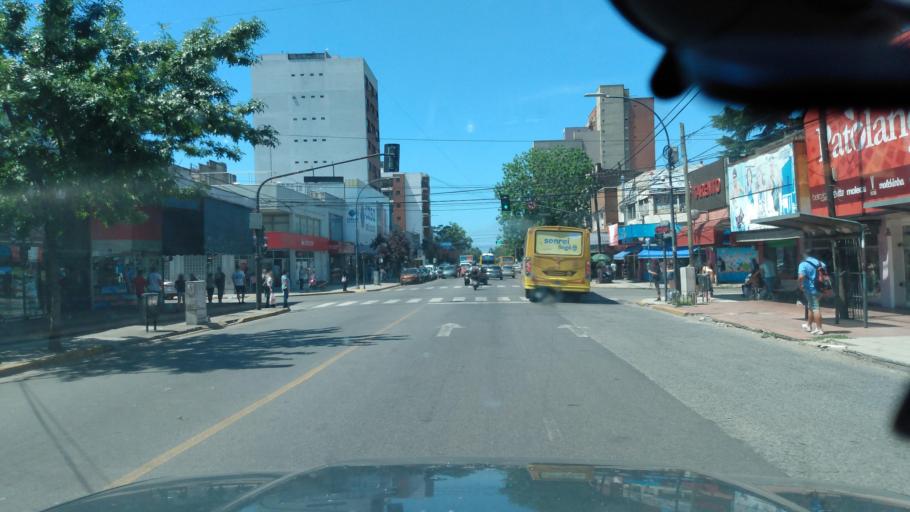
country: AR
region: Buenos Aires
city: Hurlingham
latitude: -34.5418
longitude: -58.7115
